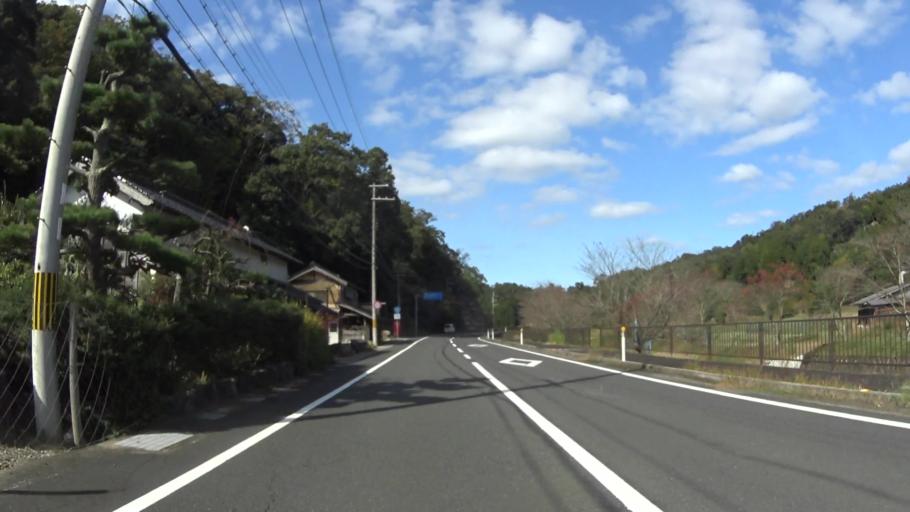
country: JP
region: Hyogo
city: Toyooka
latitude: 35.5627
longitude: 134.9785
